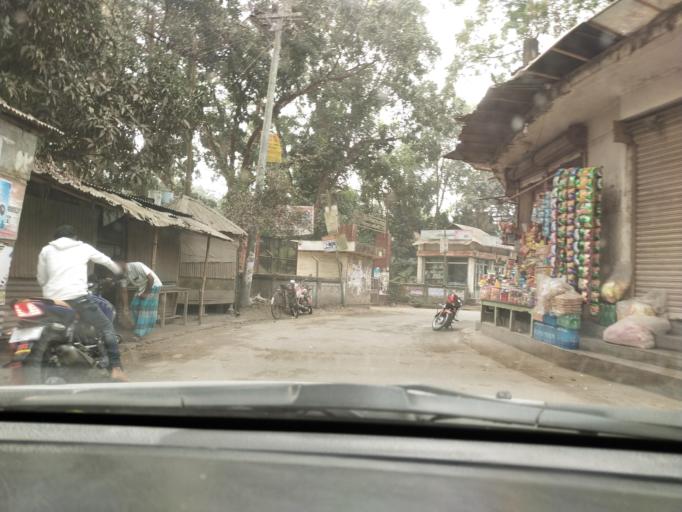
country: BD
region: Dhaka
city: Narsingdi
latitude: 24.0374
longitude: 90.7324
